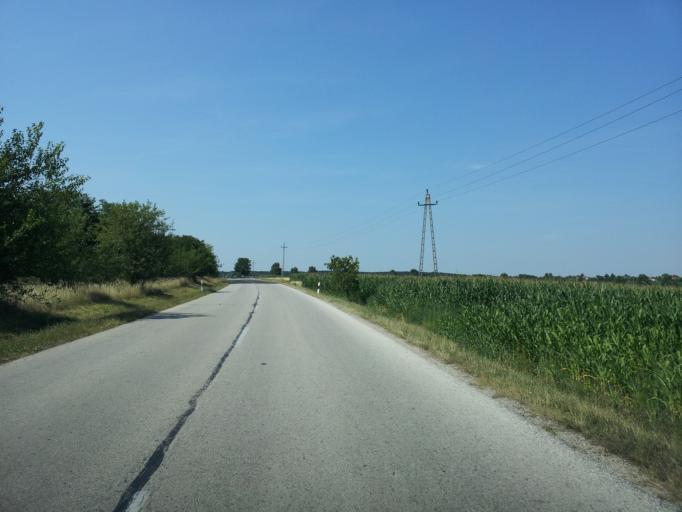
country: HU
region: Fejer
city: Pakozd
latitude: 47.2617
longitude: 18.5206
